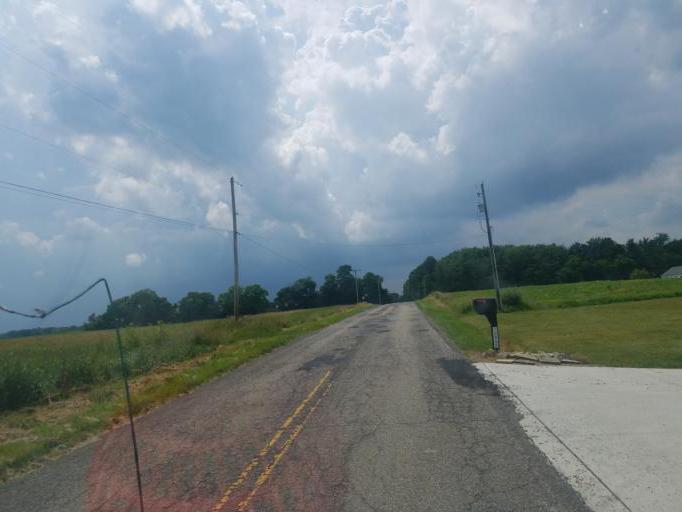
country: US
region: Ohio
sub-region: Columbiana County
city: Salem
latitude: 40.9739
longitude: -80.8930
